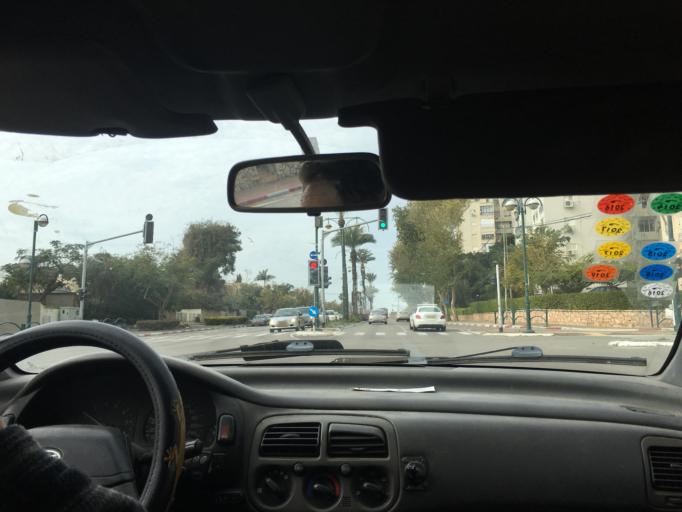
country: IL
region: Tel Aviv
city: Ramat HaSharon
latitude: 32.1371
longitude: 34.8415
